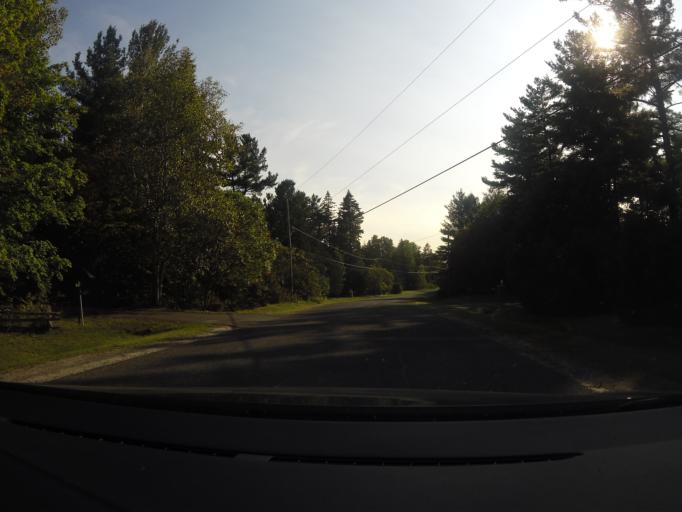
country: CA
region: Ontario
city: Carleton Place
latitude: 45.2866
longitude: -76.1086
